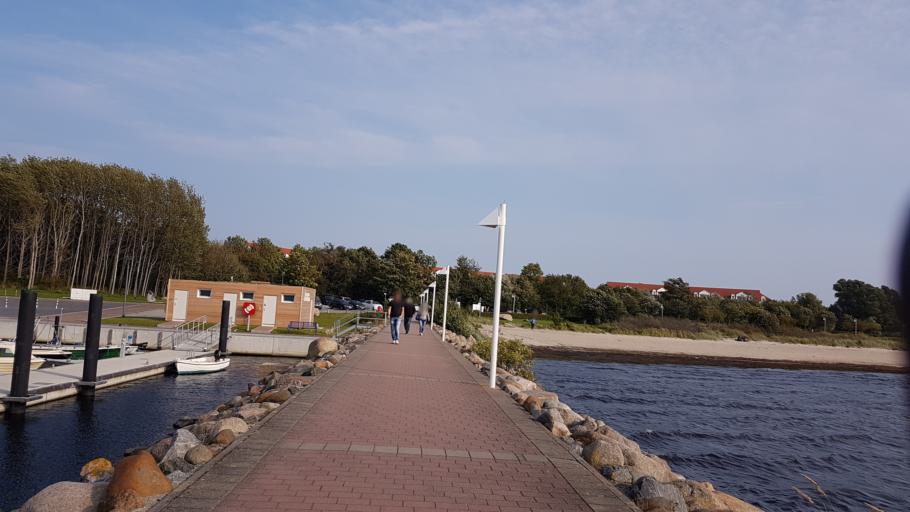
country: DE
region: Mecklenburg-Vorpommern
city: Glowe
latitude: 54.5735
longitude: 13.4683
